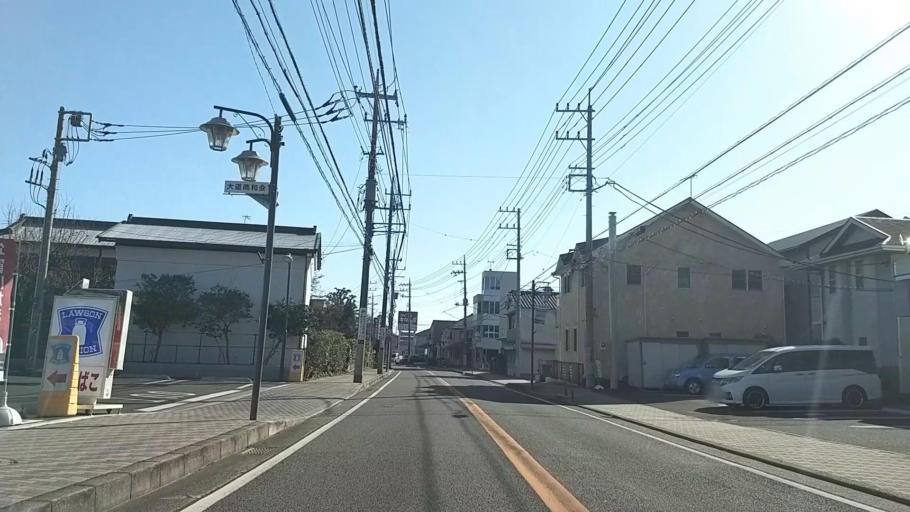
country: JP
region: Kanagawa
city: Hadano
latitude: 35.3785
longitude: 139.2216
